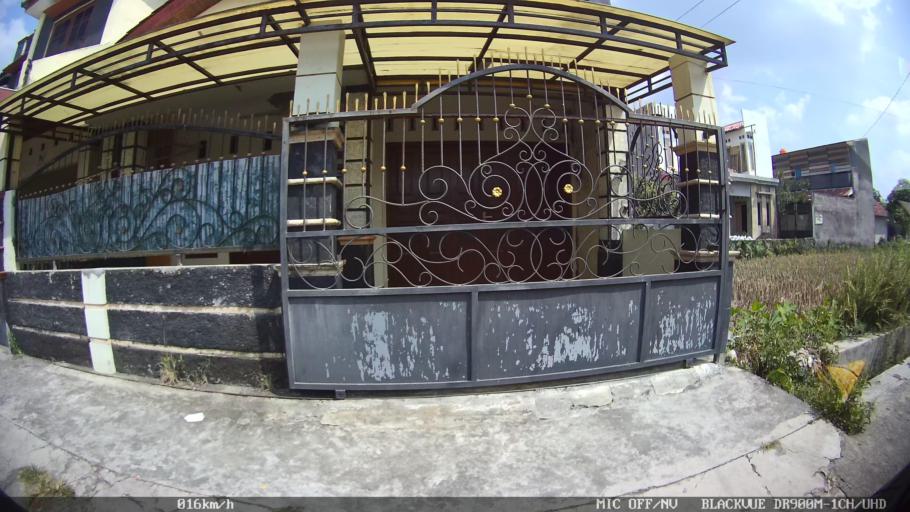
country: ID
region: Daerah Istimewa Yogyakarta
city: Yogyakarta
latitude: -7.8075
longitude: 110.4039
